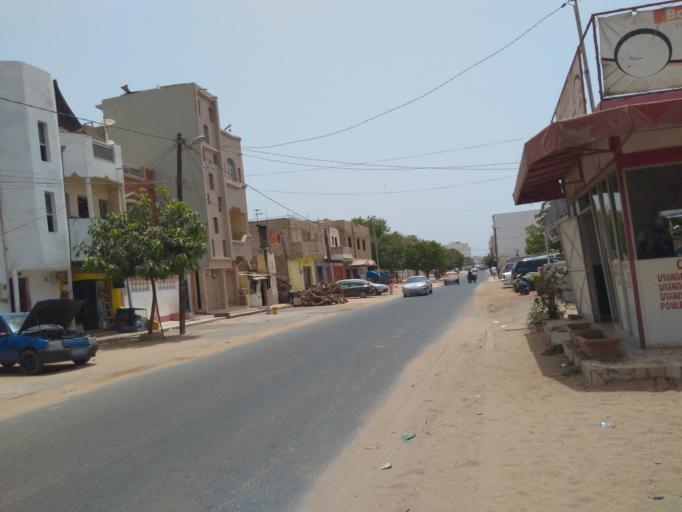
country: SN
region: Dakar
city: Grand Dakar
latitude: 14.7241
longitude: -17.4653
